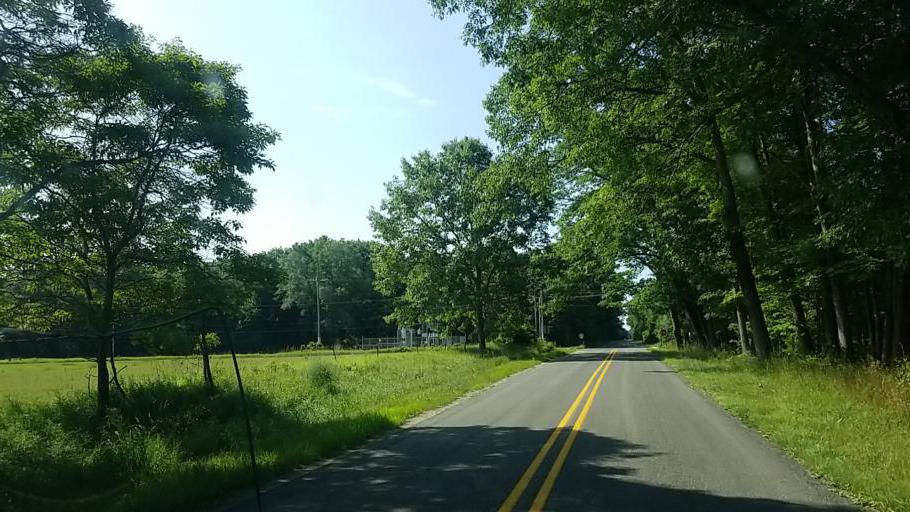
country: US
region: Michigan
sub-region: Muskegon County
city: Whitehall
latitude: 43.3575
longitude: -86.3763
